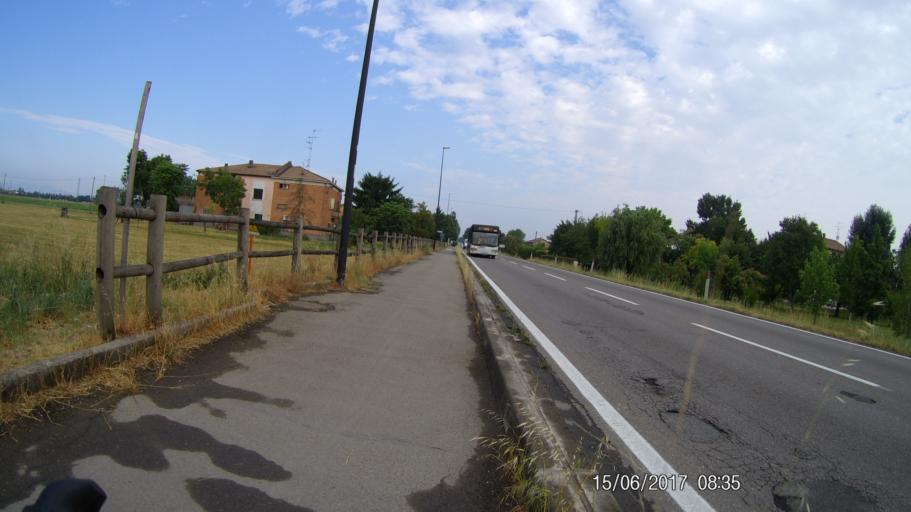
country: IT
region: Emilia-Romagna
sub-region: Provincia di Reggio Emilia
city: Cade-Gaida
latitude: 44.7323
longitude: 10.5337
